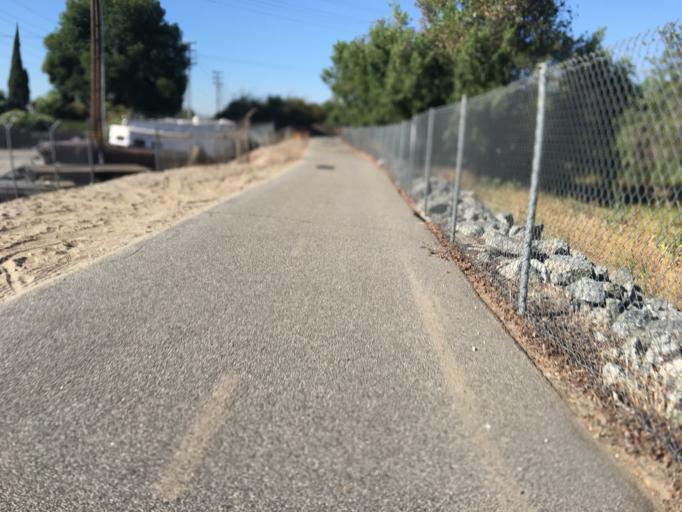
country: US
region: California
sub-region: Los Angeles County
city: West Whittier-Los Nietos
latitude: 34.0063
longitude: -118.0681
